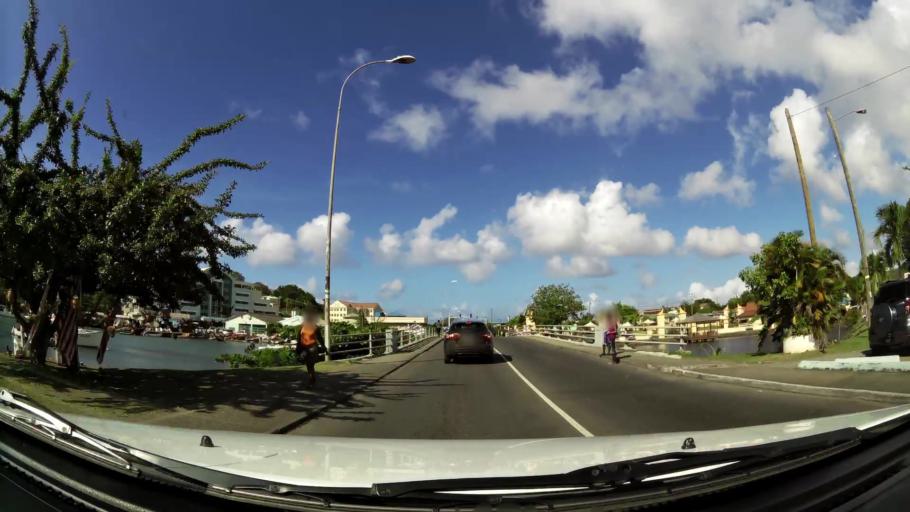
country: LC
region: Castries Quarter
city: Bisee
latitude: 14.0148
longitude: -60.9916
